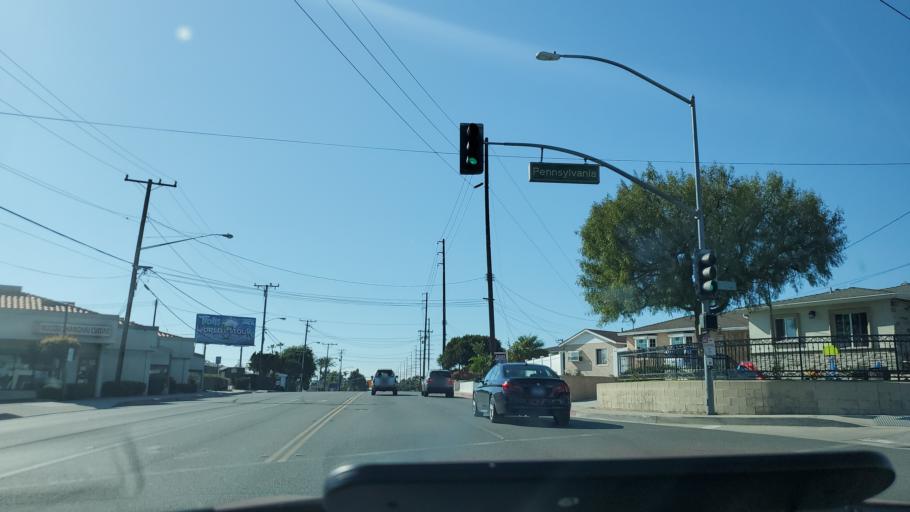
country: US
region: California
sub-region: Los Angeles County
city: Lomita
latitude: 33.8048
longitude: -118.3254
